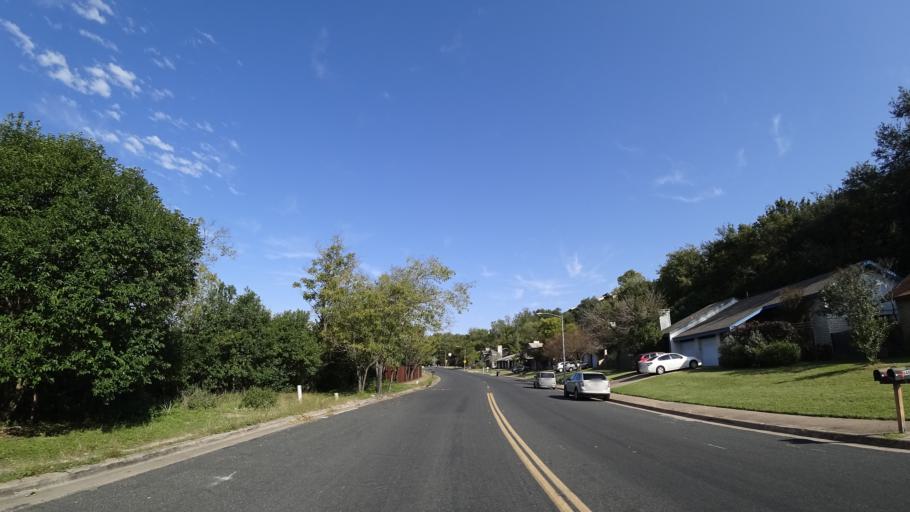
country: US
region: Texas
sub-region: Travis County
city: West Lake Hills
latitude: 30.3474
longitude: -97.7561
